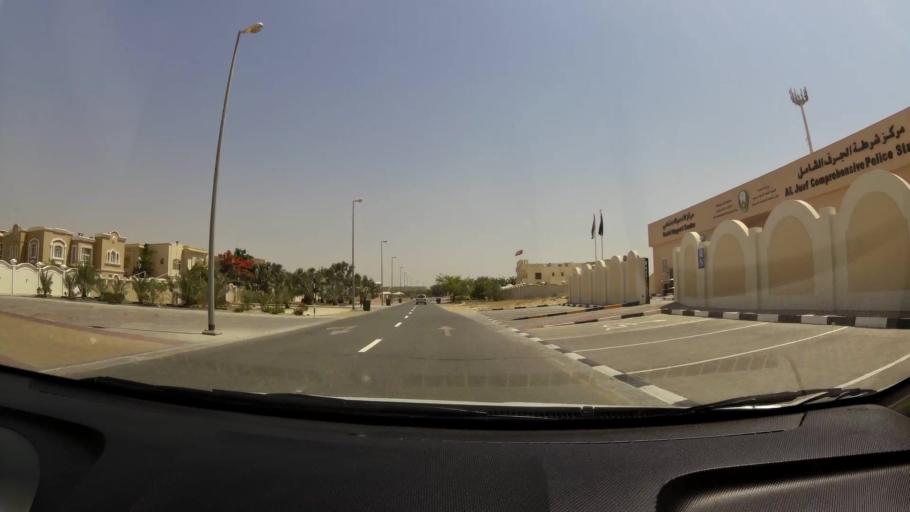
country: AE
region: Ajman
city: Ajman
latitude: 25.4246
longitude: 55.5084
